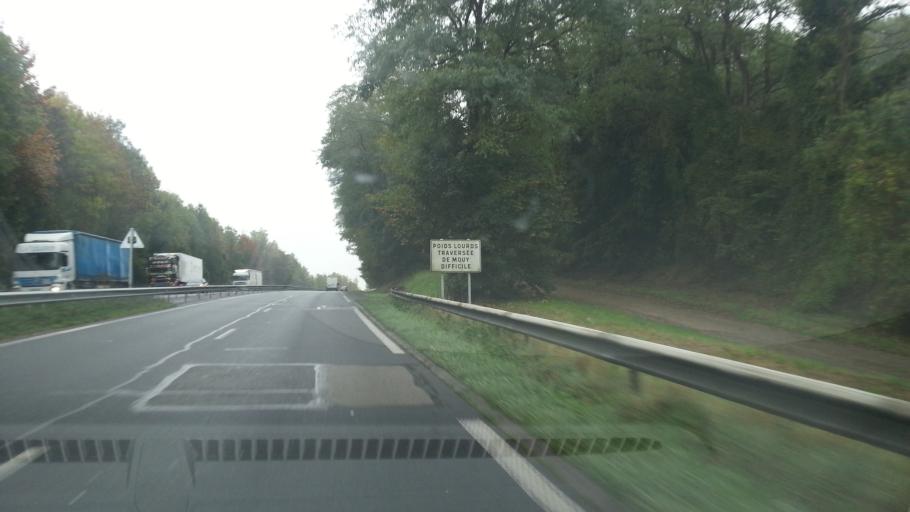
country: FR
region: Picardie
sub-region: Departement de l'Oise
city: Rantigny
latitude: 49.3282
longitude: 2.4360
